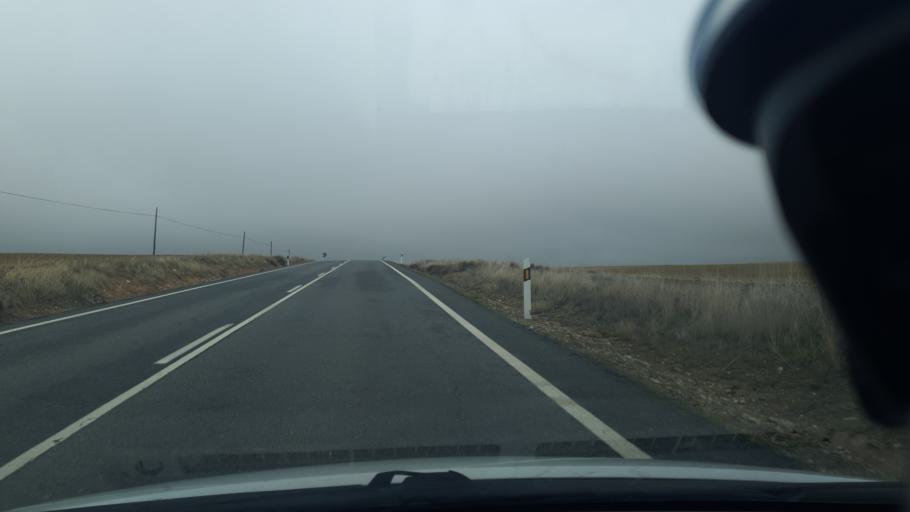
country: ES
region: Castille and Leon
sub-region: Provincia de Segovia
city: Encinillas
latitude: 41.0388
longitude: -4.1365
